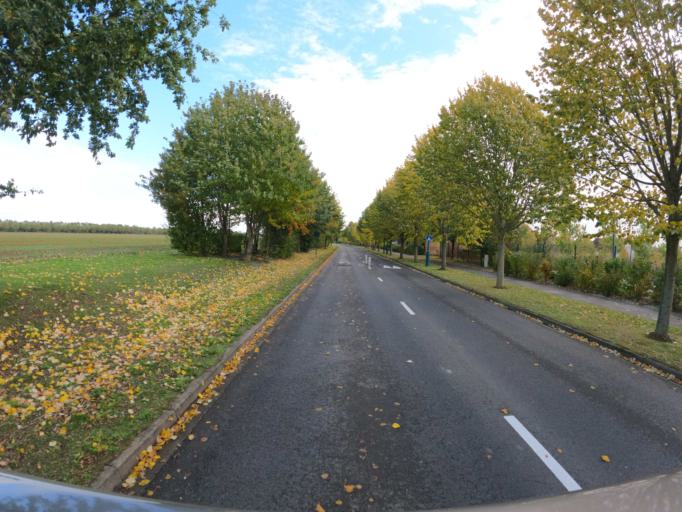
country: FR
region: Ile-de-France
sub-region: Departement de Seine-et-Marne
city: Magny-le-Hongre
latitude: 48.8784
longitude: 2.8095
